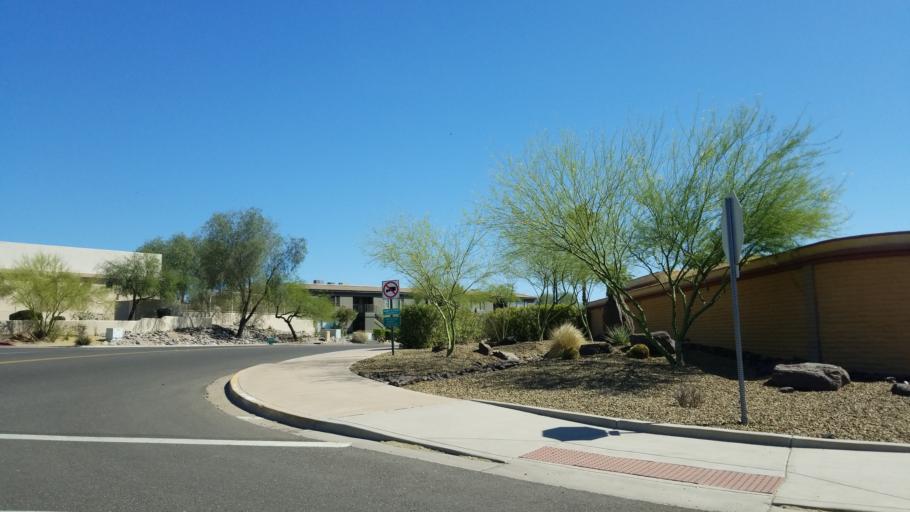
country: US
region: Arizona
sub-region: Maricopa County
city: Fountain Hills
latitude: 33.6086
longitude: -111.7198
